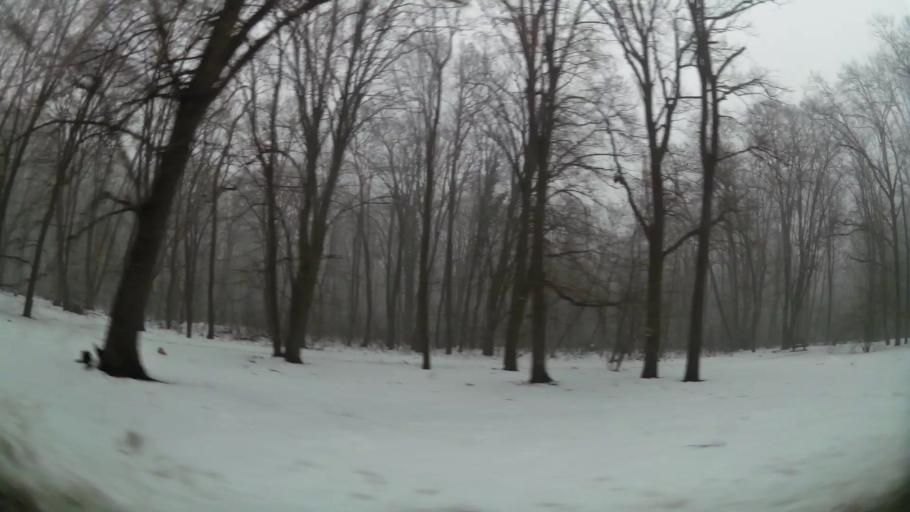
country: RS
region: Central Serbia
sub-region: Belgrade
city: Cukarica
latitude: 44.7723
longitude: 20.4282
